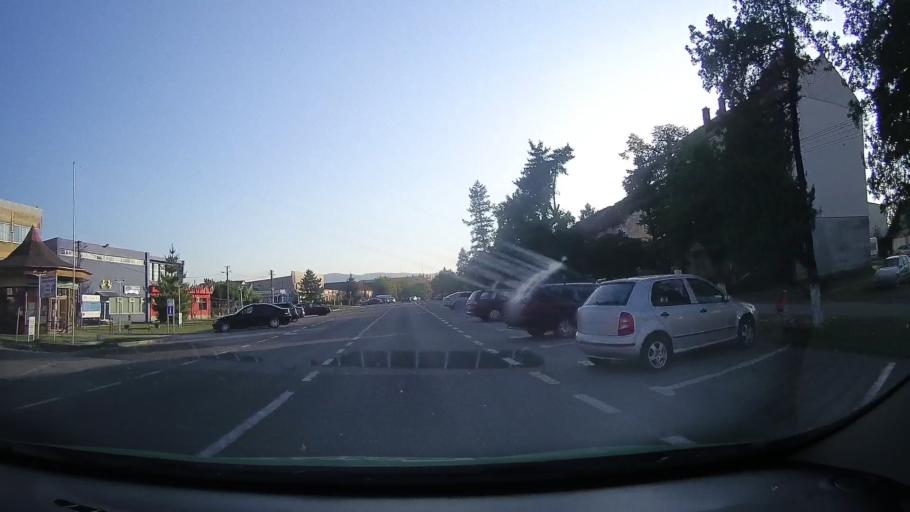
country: RO
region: Arad
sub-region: Comuna Pancota
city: Pancota
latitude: 46.3250
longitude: 21.6888
